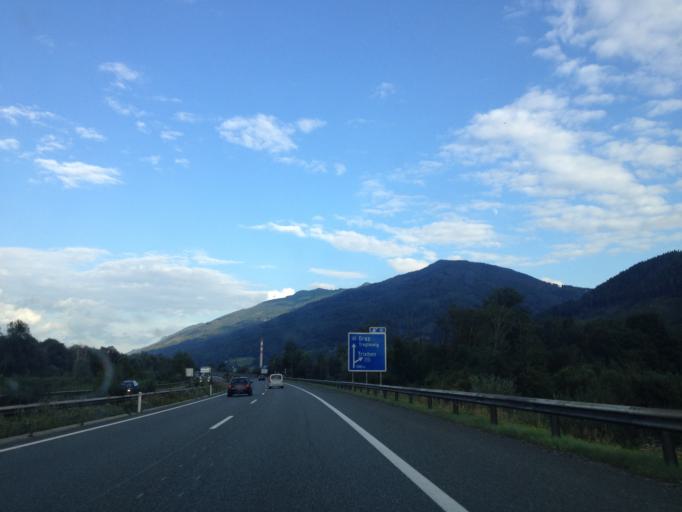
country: AT
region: Styria
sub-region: Politischer Bezirk Liezen
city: Trieben
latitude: 47.4992
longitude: 14.4643
